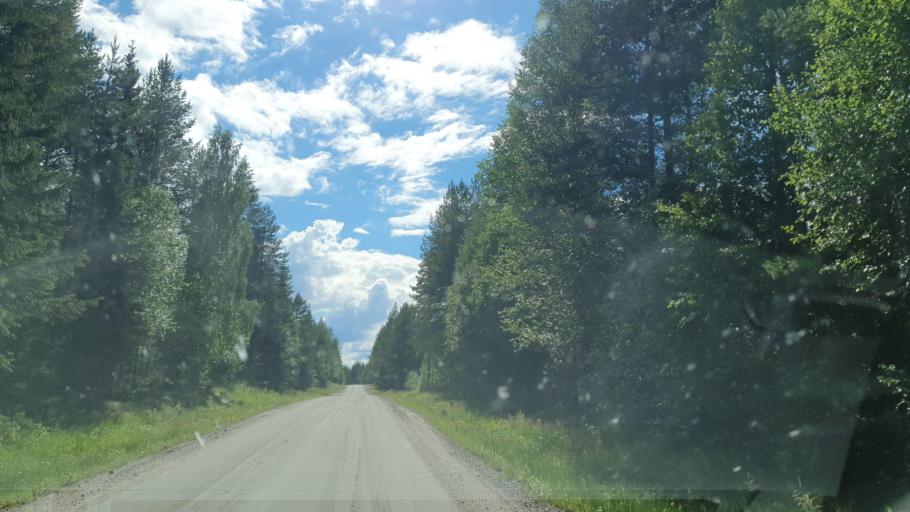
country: FI
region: Kainuu
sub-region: Kehys-Kainuu
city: Kuhmo
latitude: 64.1456
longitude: 29.7112
